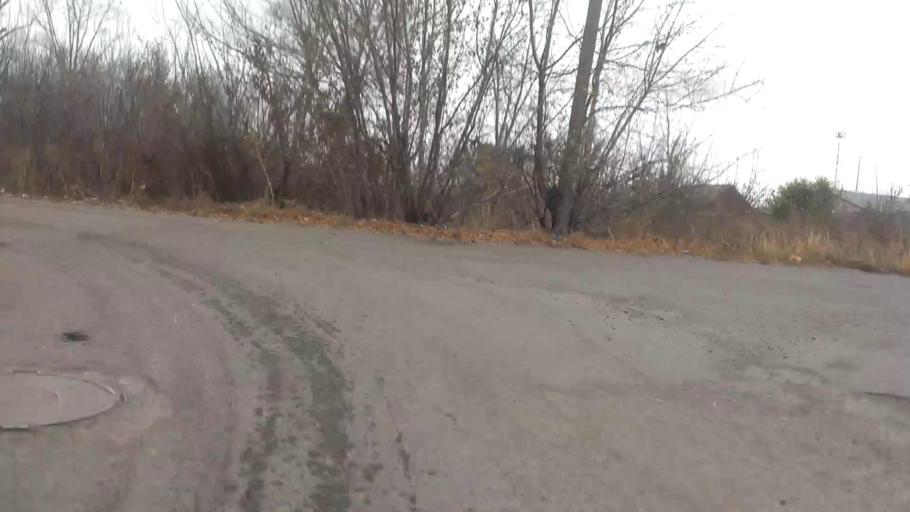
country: RU
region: Altai Krai
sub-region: Gorod Barnaulskiy
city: Barnaul
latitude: 53.3543
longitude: 83.7544
